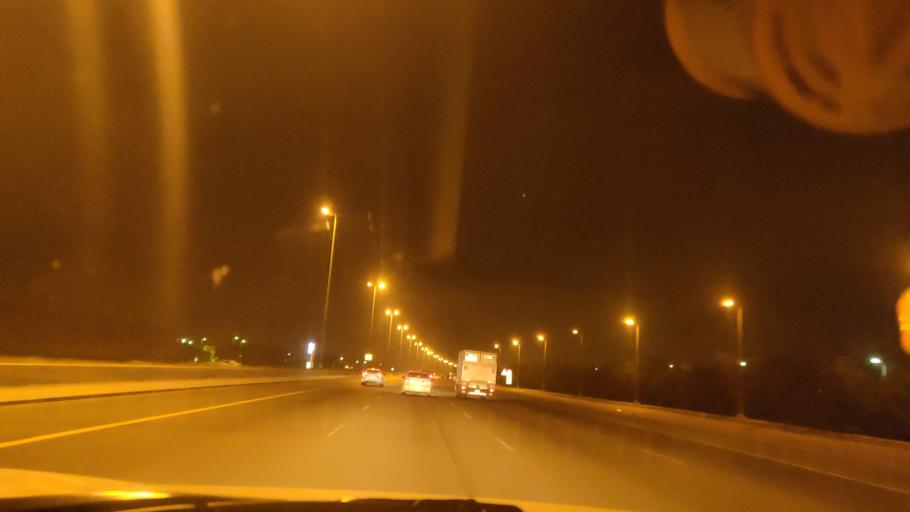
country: KW
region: Al Ahmadi
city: Ar Riqqah
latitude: 29.1429
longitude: 48.0853
